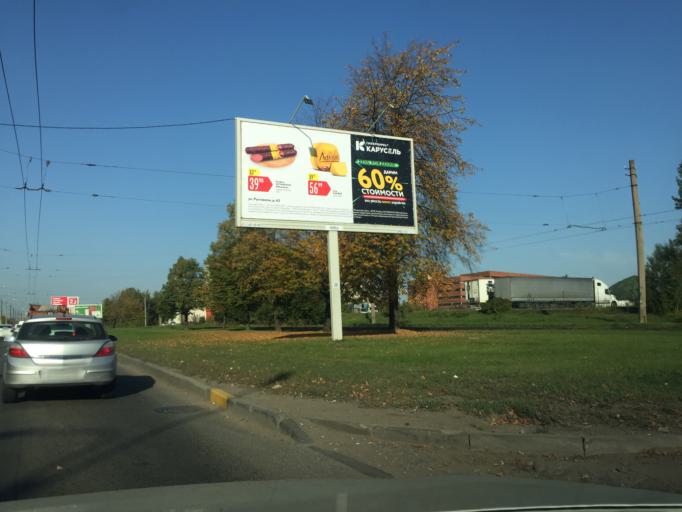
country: RU
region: Leningrad
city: Akademicheskoe
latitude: 59.9994
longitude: 30.4374
